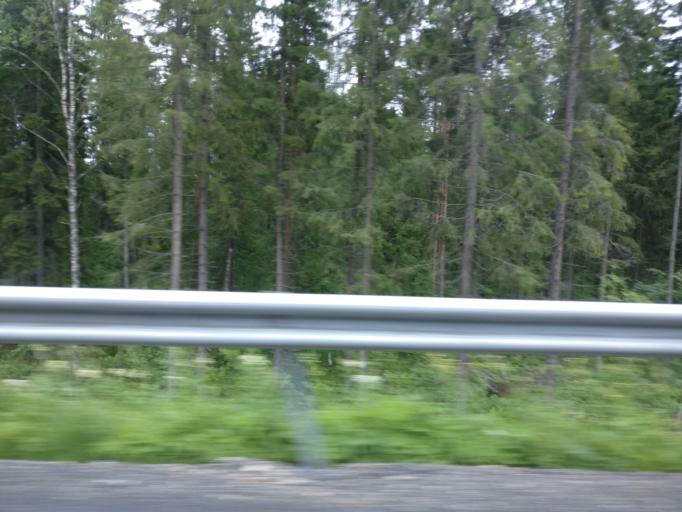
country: FI
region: Northern Savo
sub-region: Varkaus
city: Leppaevirta
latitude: 62.6134
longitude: 27.6229
